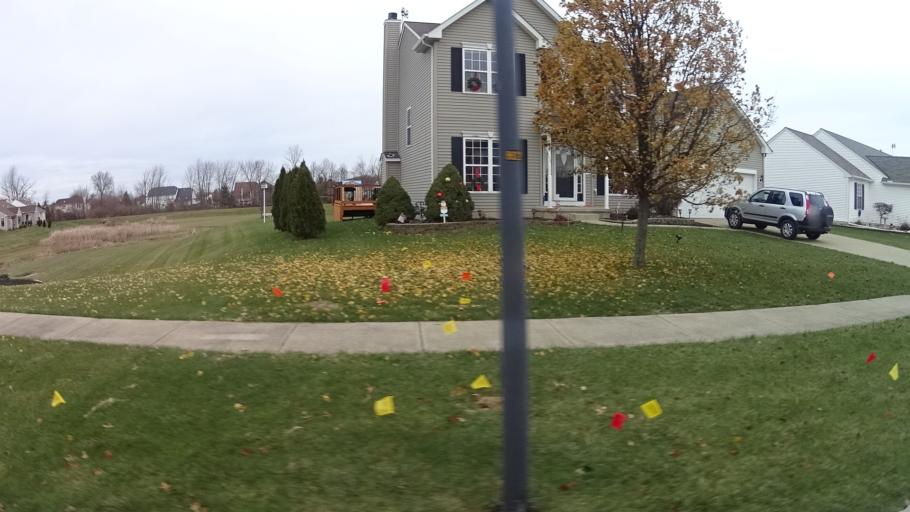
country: US
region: Ohio
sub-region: Lorain County
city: Sheffield
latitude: 41.4171
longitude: -82.0566
